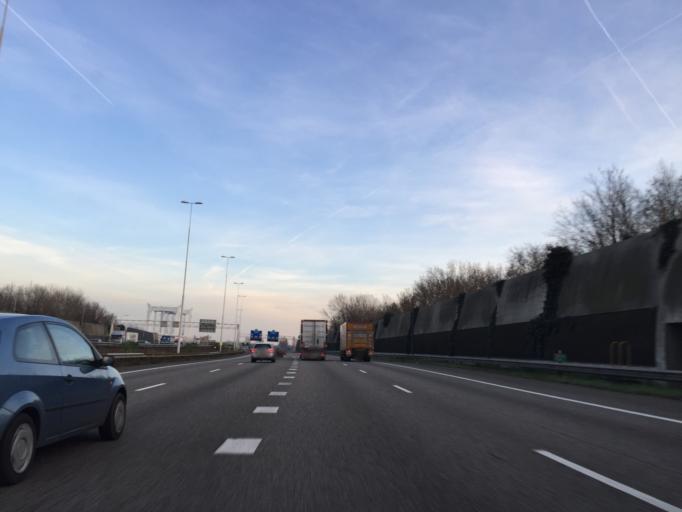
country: NL
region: South Holland
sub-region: Gemeente Zwijndrecht
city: Zwijndrecht
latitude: 51.8130
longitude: 4.6372
